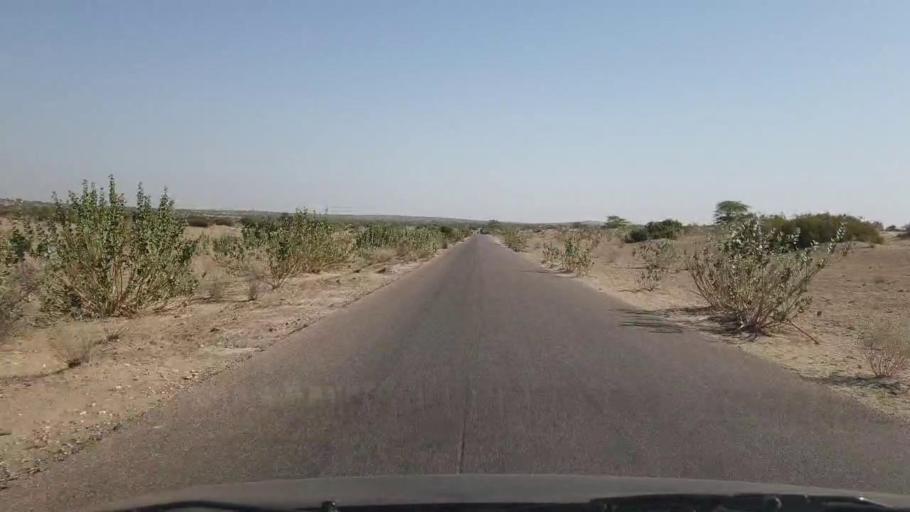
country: PK
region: Sindh
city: Chor
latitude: 25.4936
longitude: 69.8061
